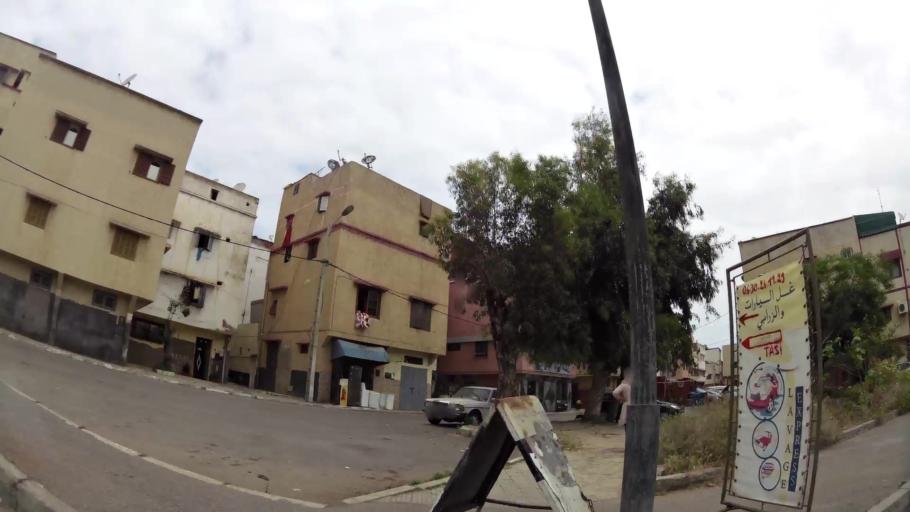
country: MA
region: Rabat-Sale-Zemmour-Zaer
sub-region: Rabat
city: Rabat
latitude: 34.0002
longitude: -6.8657
